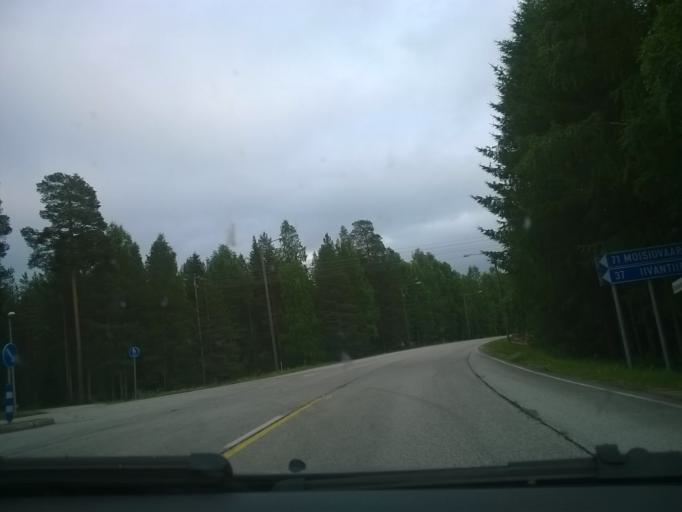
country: FI
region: Kainuu
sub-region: Kehys-Kainuu
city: Kuhmo
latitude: 64.1371
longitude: 29.4549
